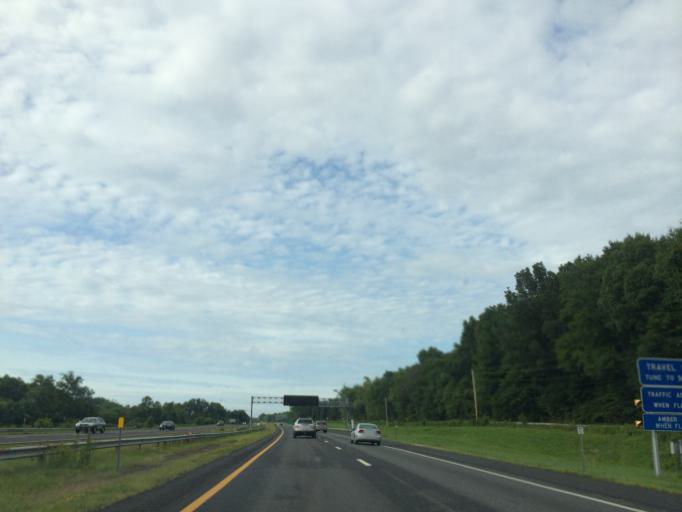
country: US
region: New York
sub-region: Ulster County
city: Lake Katrine
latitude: 41.9728
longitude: -74.0126
